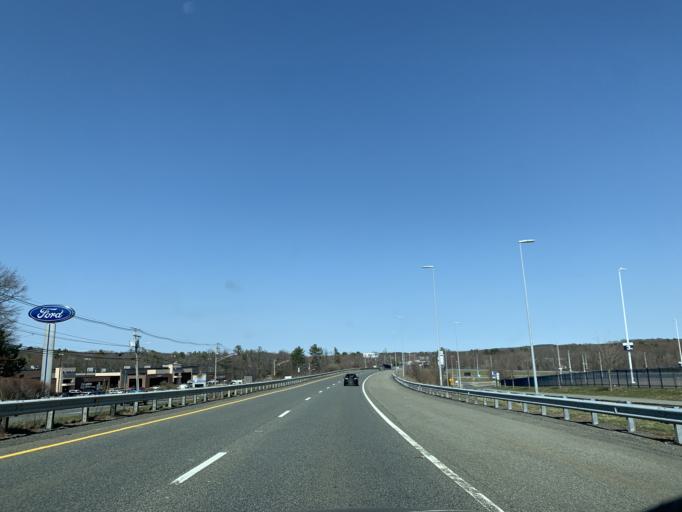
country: US
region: Massachusetts
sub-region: Norfolk County
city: Foxborough
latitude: 42.0952
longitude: -71.2675
